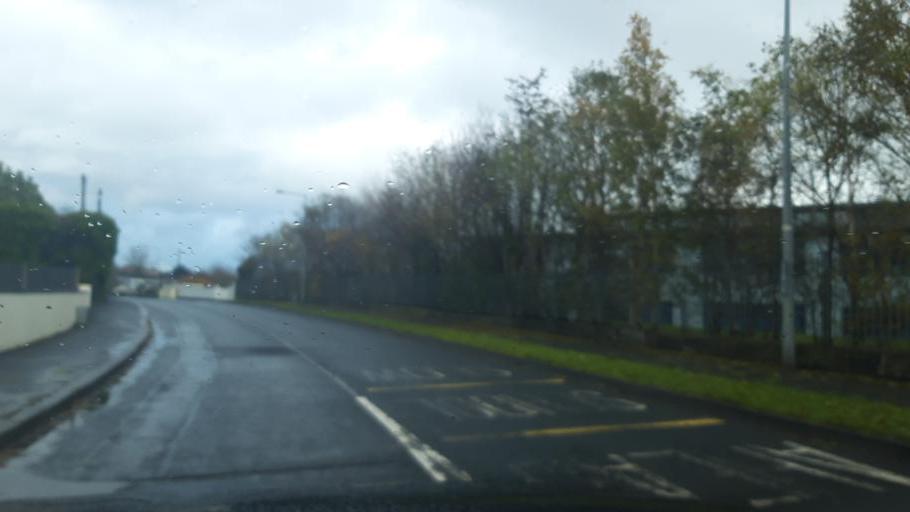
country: IE
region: Leinster
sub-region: Wicklow
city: Kilcoole
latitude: 53.1007
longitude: -6.0662
